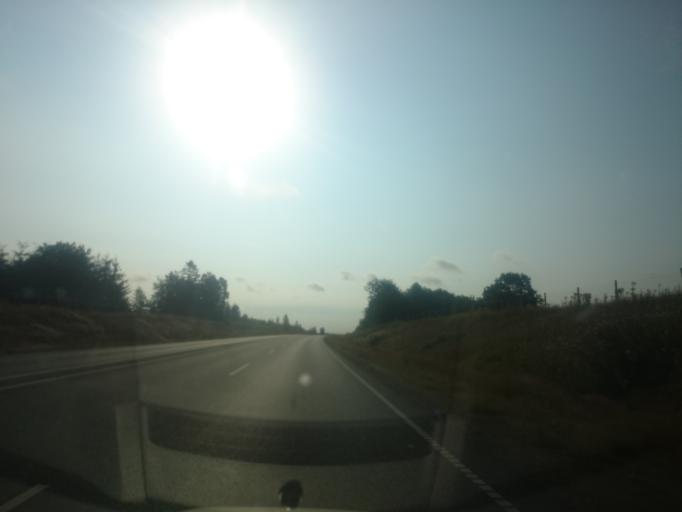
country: DK
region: South Denmark
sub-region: Vejle Kommune
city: Egtved
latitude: 55.7038
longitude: 9.2919
